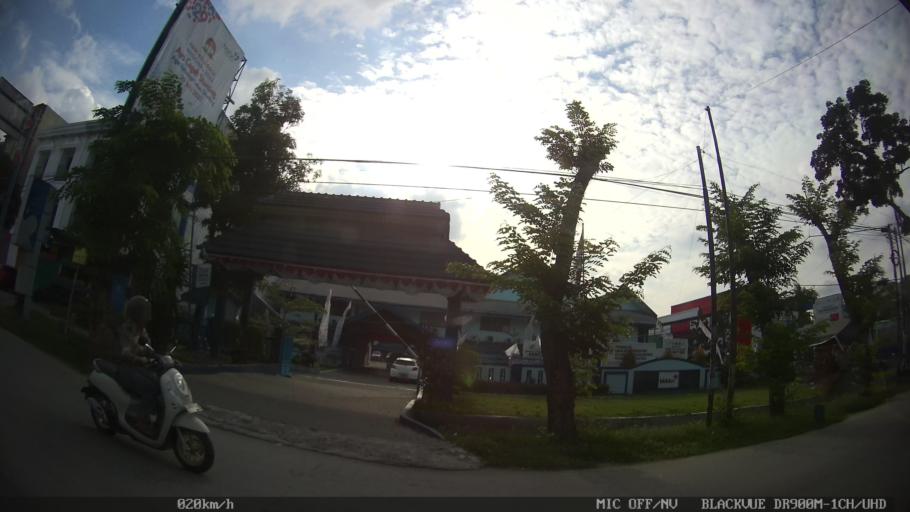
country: ID
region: North Sumatra
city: Medan
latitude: 3.6277
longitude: 98.6809
